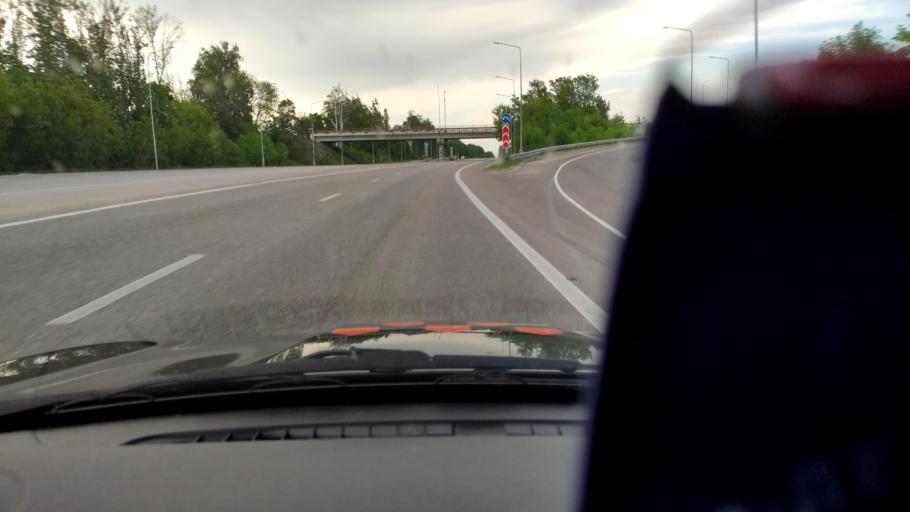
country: RU
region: Voronezj
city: Kolodeznyy
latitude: 51.3378
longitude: 39.0241
